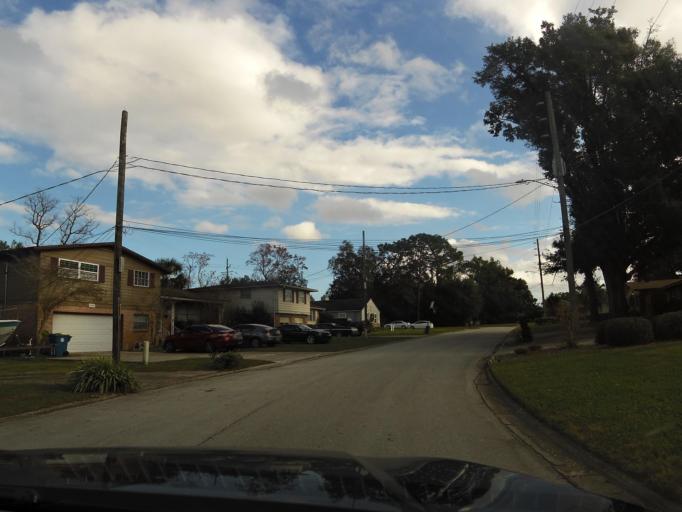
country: US
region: Florida
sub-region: Duval County
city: Jacksonville
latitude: 30.3429
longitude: -81.5785
